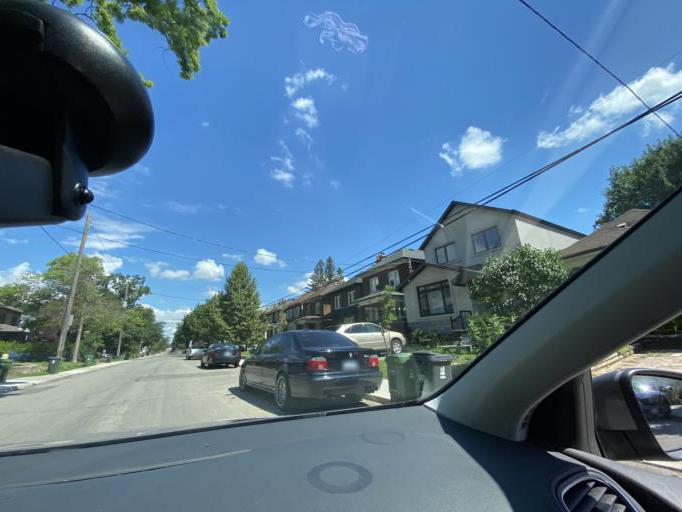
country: CA
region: Ontario
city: Etobicoke
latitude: 43.6603
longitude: -79.4929
